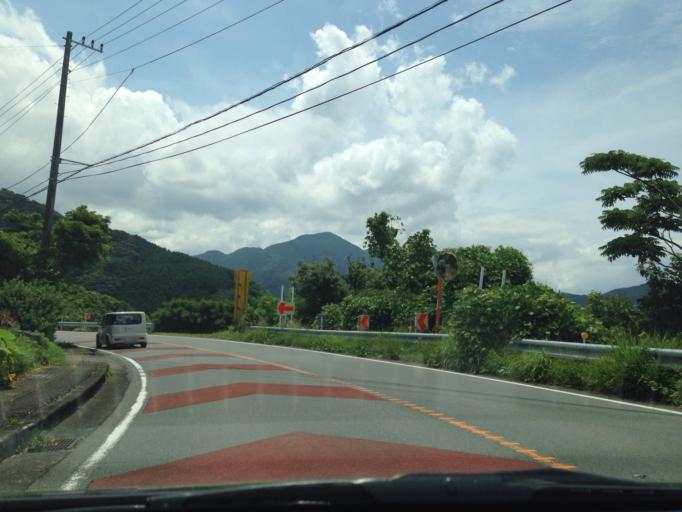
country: JP
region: Shizuoka
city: Heda
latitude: 34.8650
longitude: 138.7630
